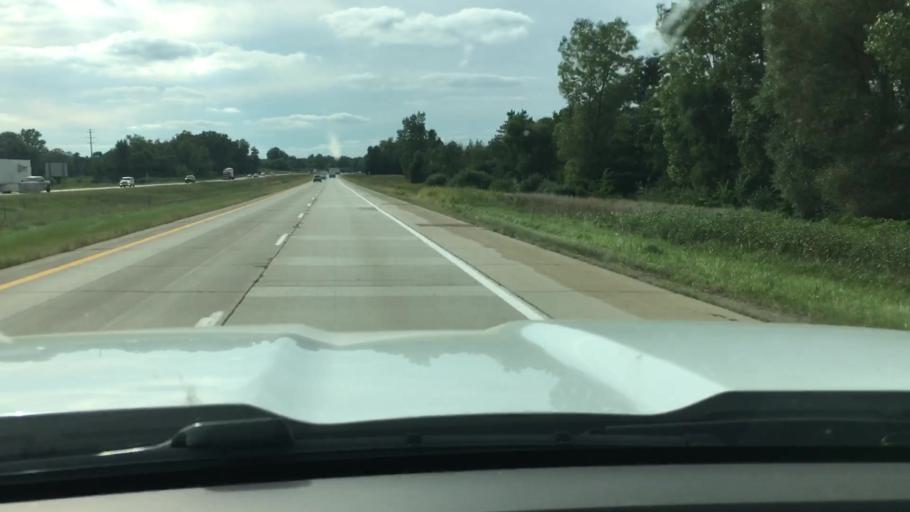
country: US
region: Michigan
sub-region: Lapeer County
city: Lapeer
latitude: 43.0119
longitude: -83.2683
